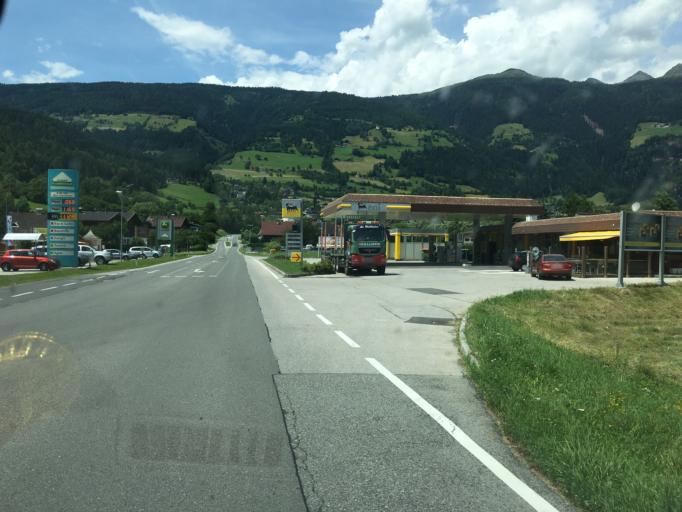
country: AT
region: Carinthia
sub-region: Politischer Bezirk Spittal an der Drau
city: Winklern
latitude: 46.8613
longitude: 12.8926
